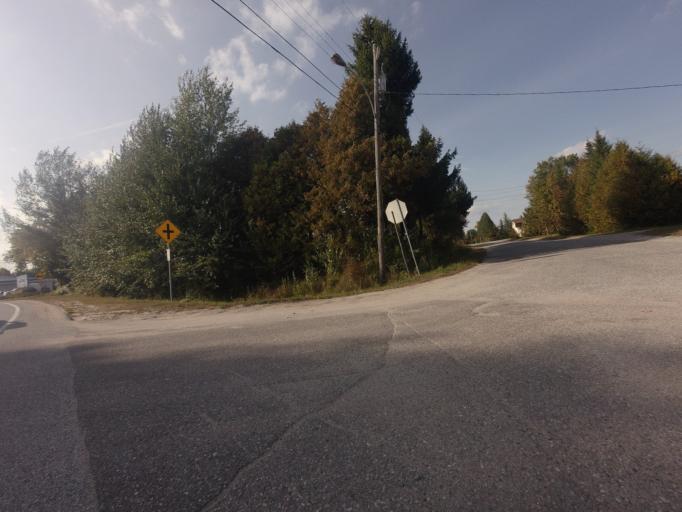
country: CA
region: Quebec
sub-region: Outaouais
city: Maniwaki
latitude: 46.3851
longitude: -75.9633
